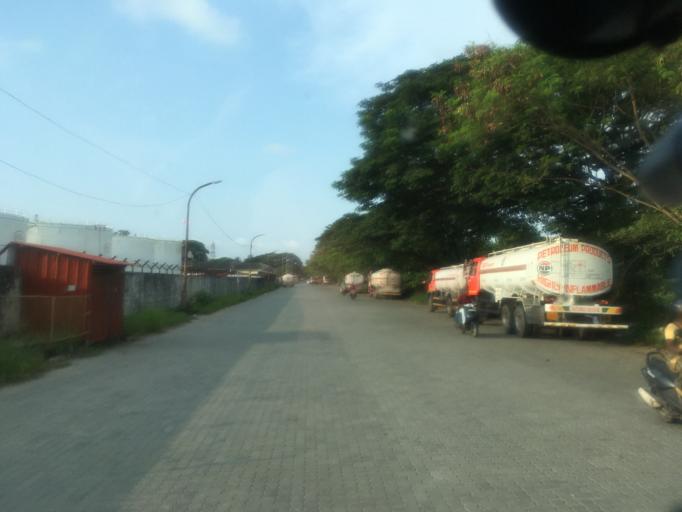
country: IN
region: Kerala
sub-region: Ernakulam
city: Cochin
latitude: 9.9493
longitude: 76.2684
